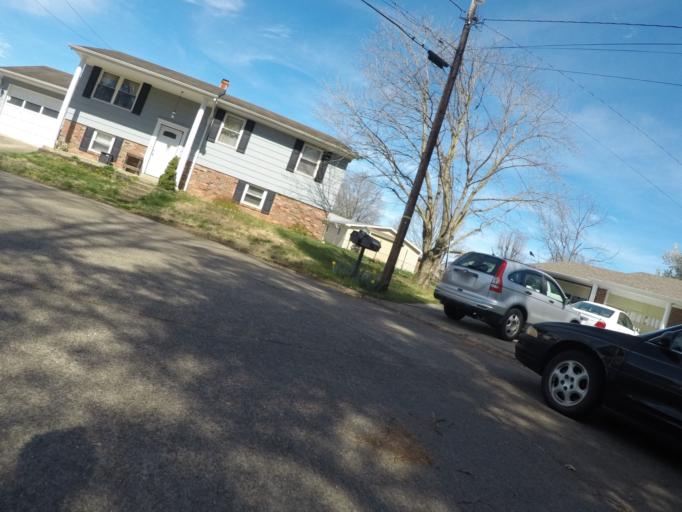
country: US
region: West Virginia
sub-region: Cabell County
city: Pea Ridge
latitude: 38.3985
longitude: -82.3147
